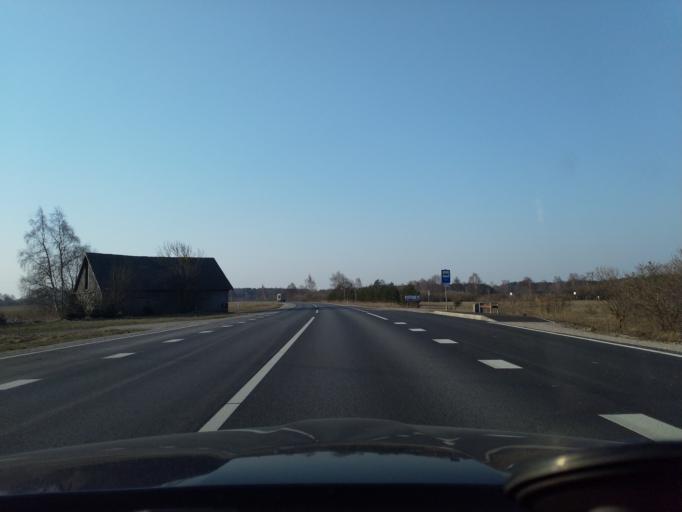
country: LV
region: Nica
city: Nica
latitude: 56.3741
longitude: 20.9983
